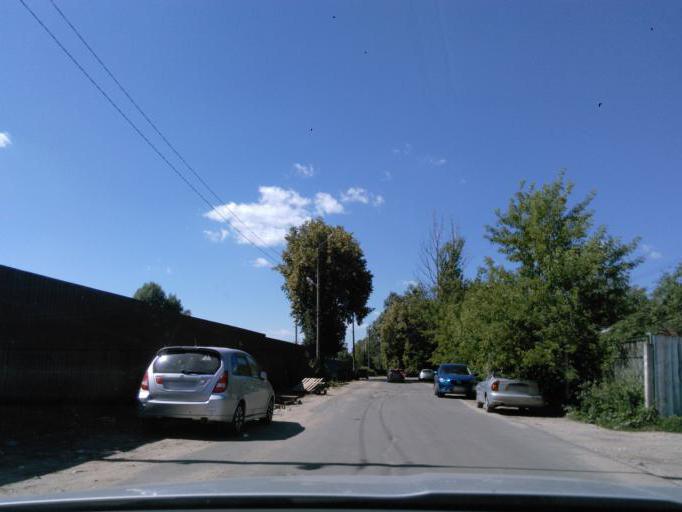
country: RU
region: Moskovskaya
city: Solnechnogorsk
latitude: 56.1850
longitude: 36.9696
